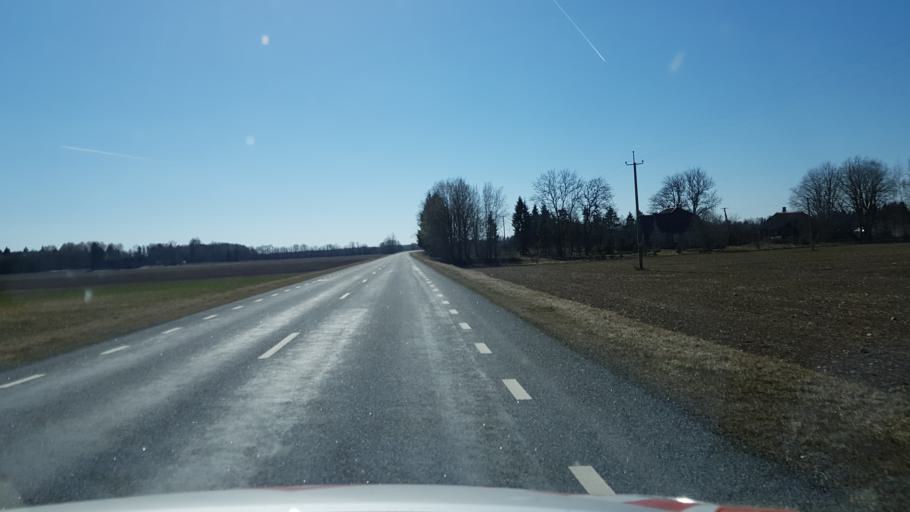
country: EE
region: Jaervamaa
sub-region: Jaerva-Jaani vald
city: Jarva-Jaani
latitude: 59.0756
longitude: 25.9550
